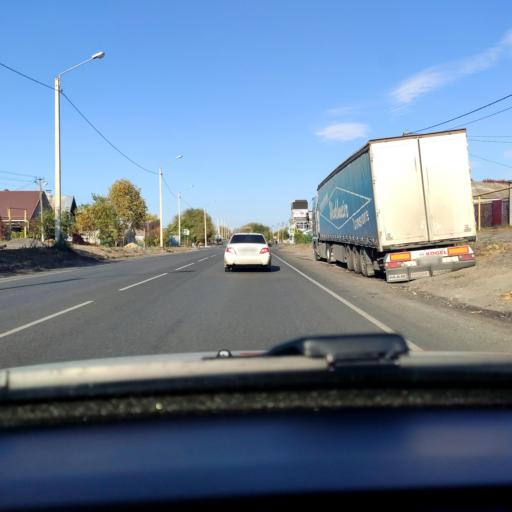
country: RU
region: Voronezj
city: Pridonskoy
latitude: 51.7109
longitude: 39.0741
